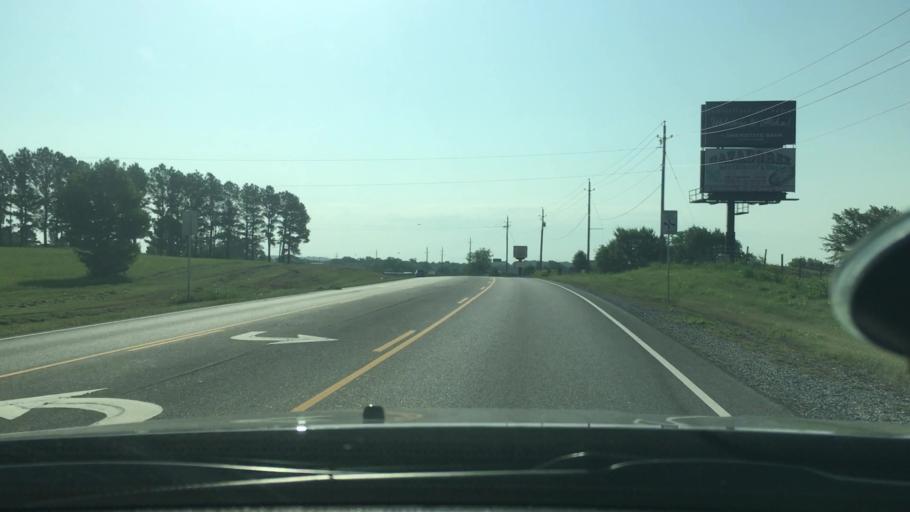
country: US
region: Oklahoma
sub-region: Atoka County
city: Atoka
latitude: 34.3944
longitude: -96.1570
